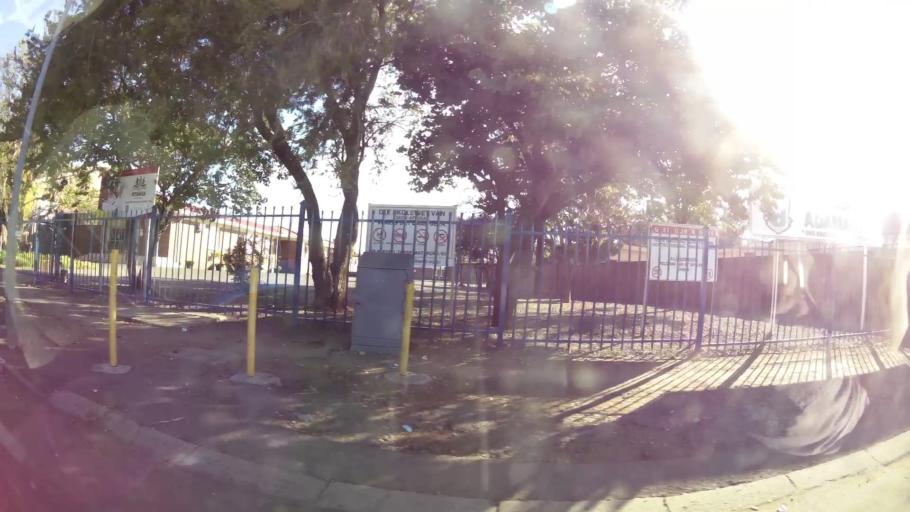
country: ZA
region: Northern Cape
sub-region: Frances Baard District Municipality
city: Kimberley
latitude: -28.7472
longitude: 24.7590
